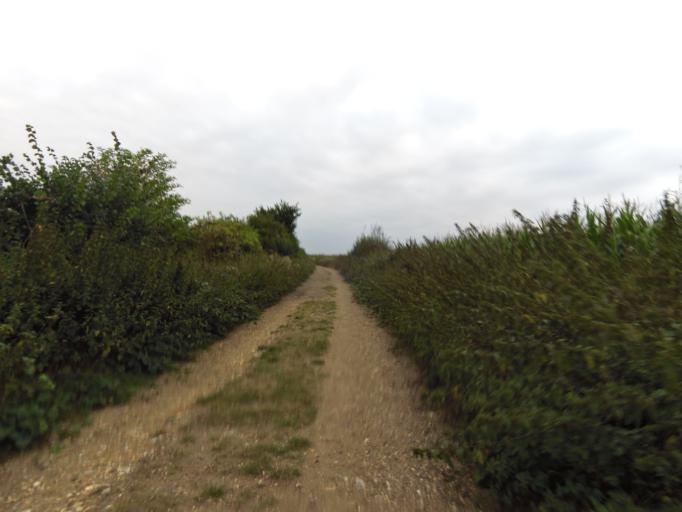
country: GB
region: England
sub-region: Hertfordshire
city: Radlett
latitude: 51.7161
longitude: -0.3118
